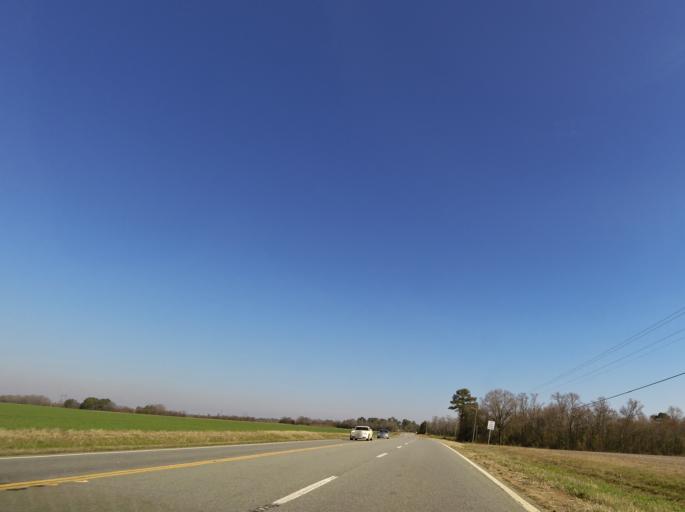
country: US
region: Georgia
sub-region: Bleckley County
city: Cochran
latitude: 32.3519
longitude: -83.3934
